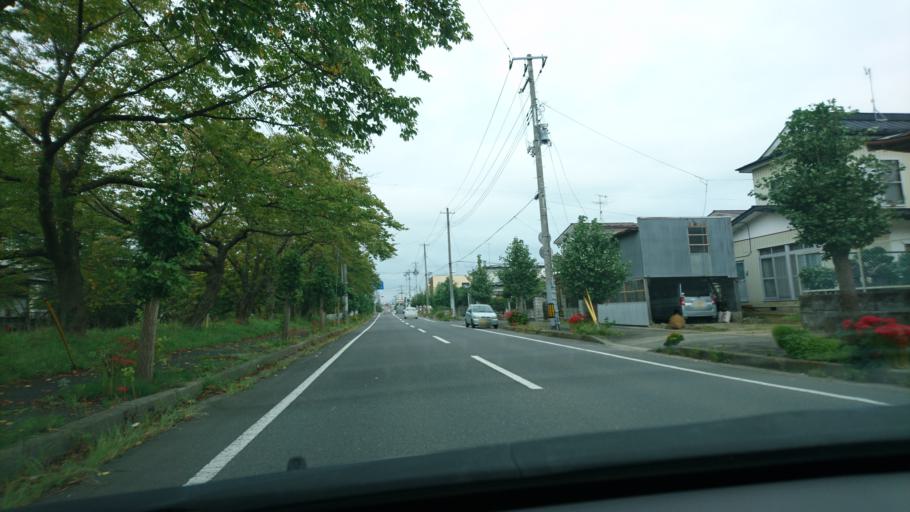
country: JP
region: Iwate
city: Ichinoseki
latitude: 38.7670
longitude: 141.1261
